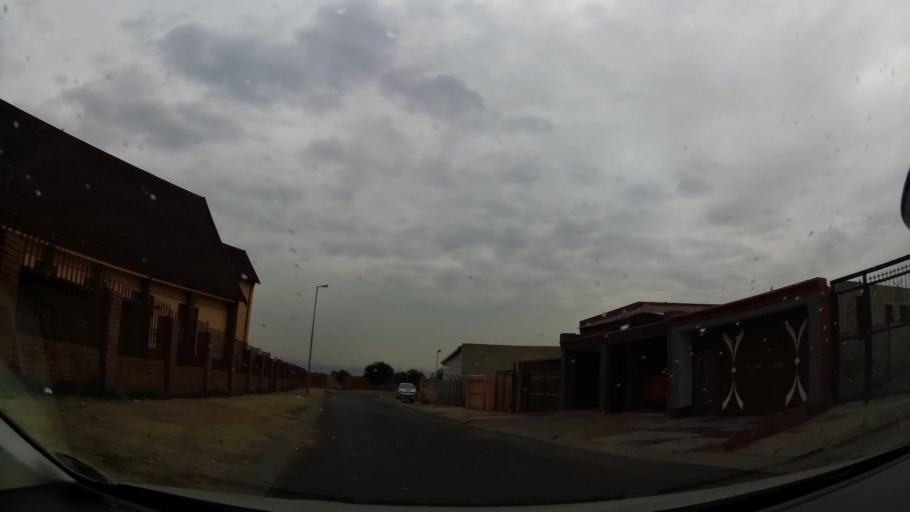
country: ZA
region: Gauteng
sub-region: City of Johannesburg Metropolitan Municipality
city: Soweto
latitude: -26.2464
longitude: 27.8758
